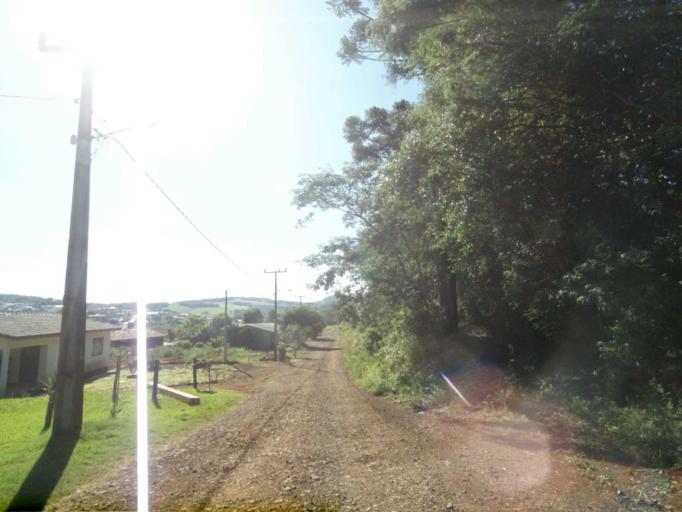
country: BR
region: Parana
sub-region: Laranjeiras Do Sul
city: Laranjeiras do Sul
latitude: -25.3794
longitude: -52.1944
